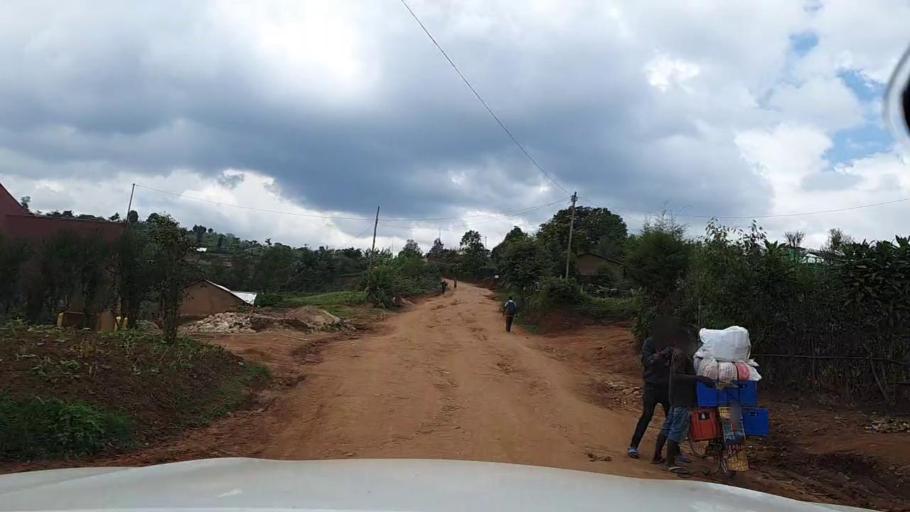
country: BI
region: Kayanza
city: Kayanza
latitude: -2.7114
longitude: 29.5322
